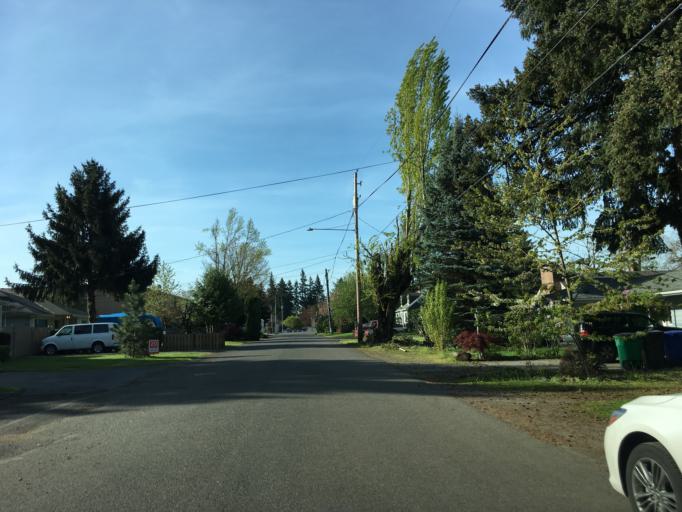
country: US
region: Oregon
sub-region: Multnomah County
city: Lents
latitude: 45.5354
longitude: -122.5535
